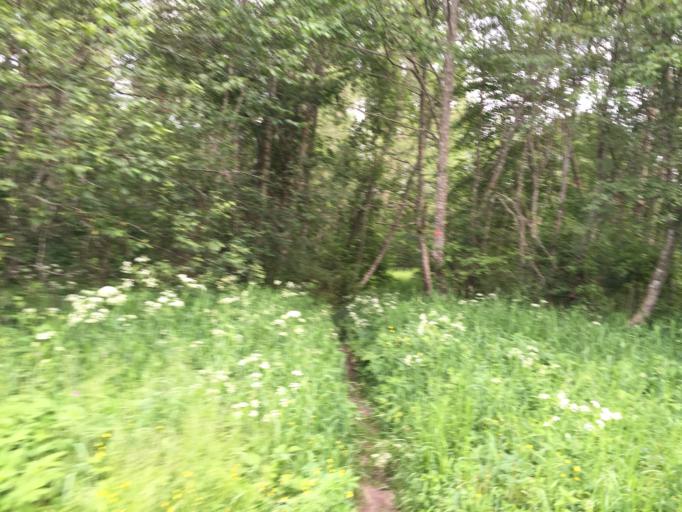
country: LV
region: Ligatne
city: Ligatne
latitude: 57.2420
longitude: 25.1468
